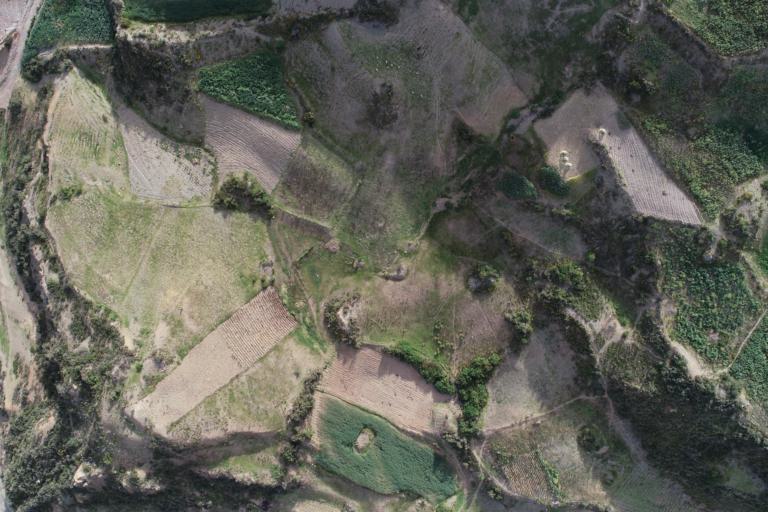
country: BO
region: La Paz
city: La Paz
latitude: -16.5489
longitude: -67.9989
